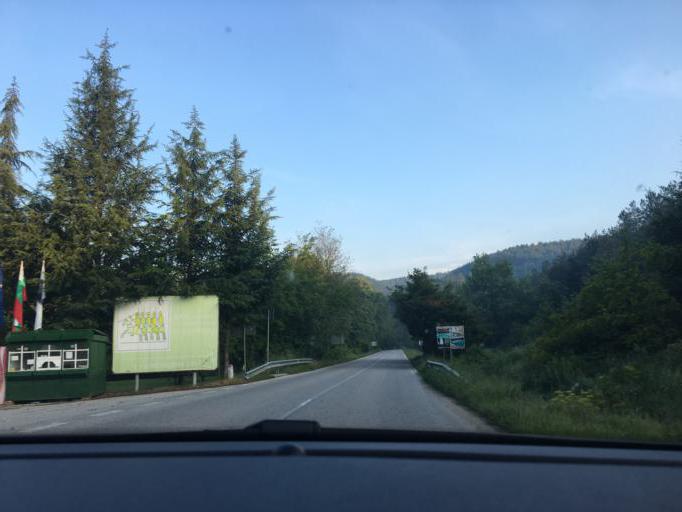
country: MK
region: Novo Selo
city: Novo Selo
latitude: 41.3951
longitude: 23.0343
